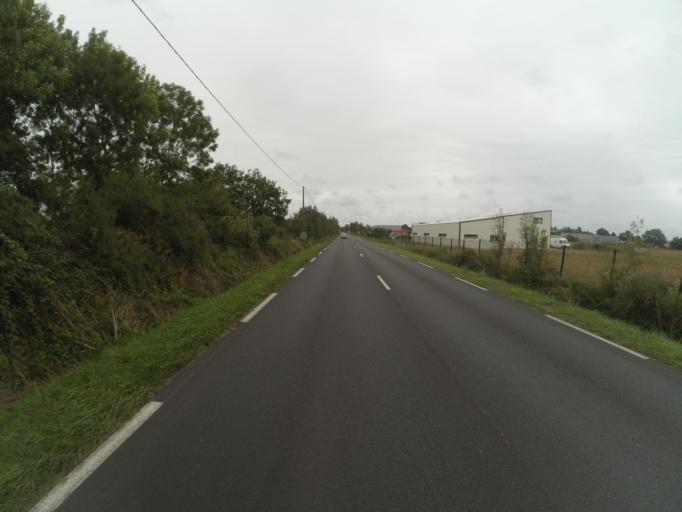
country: FR
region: Pays de la Loire
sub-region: Departement de la Vendee
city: Sallertaine
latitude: 46.8717
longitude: -1.9406
